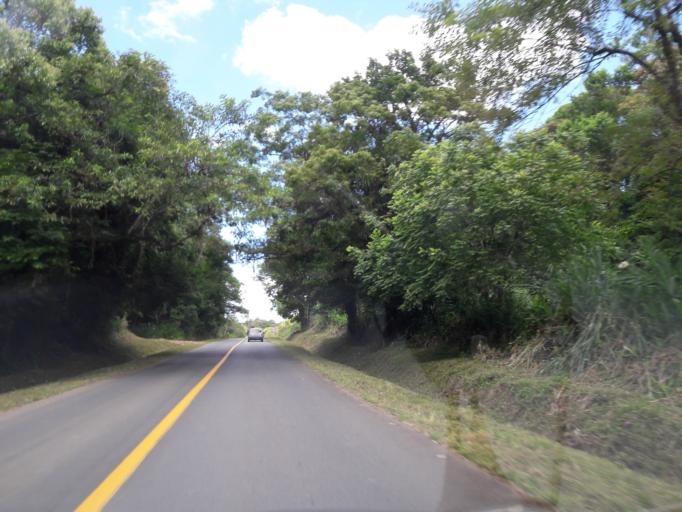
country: BR
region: Parana
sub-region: Antonina
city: Antonina
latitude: -25.4379
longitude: -48.7915
